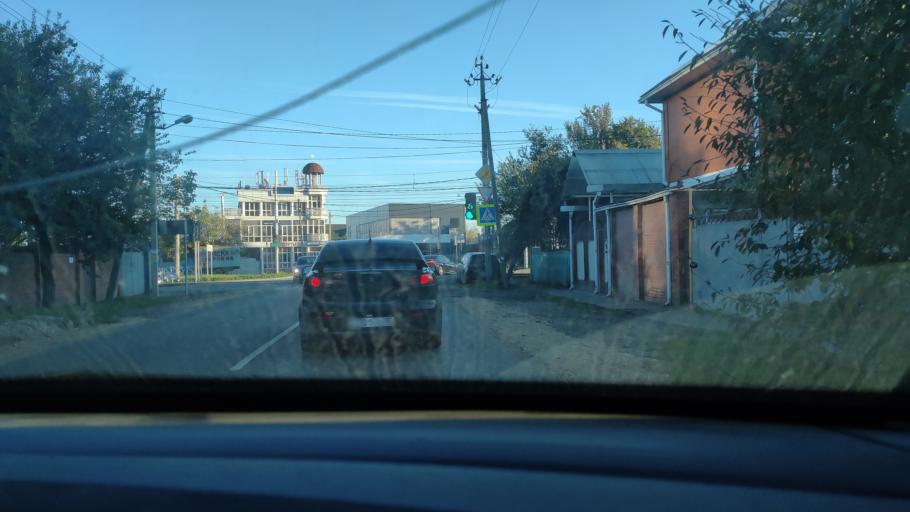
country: RU
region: Adygeya
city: Yablonovskiy
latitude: 45.0364
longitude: 38.9253
